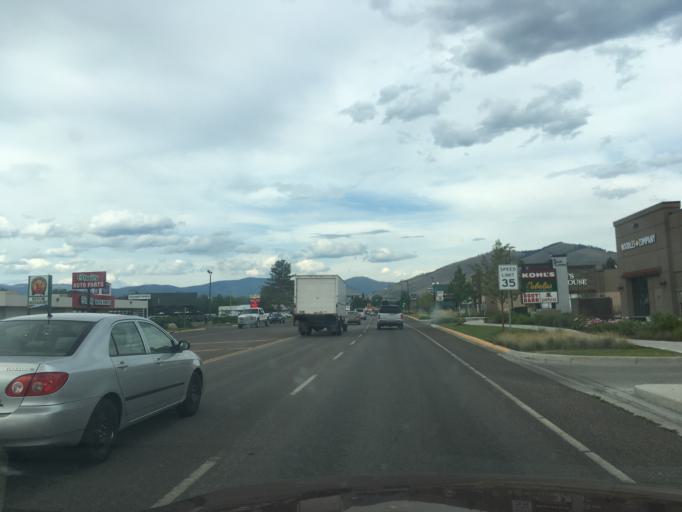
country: US
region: Montana
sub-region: Missoula County
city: Orchard Homes
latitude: 46.8369
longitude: -114.0382
